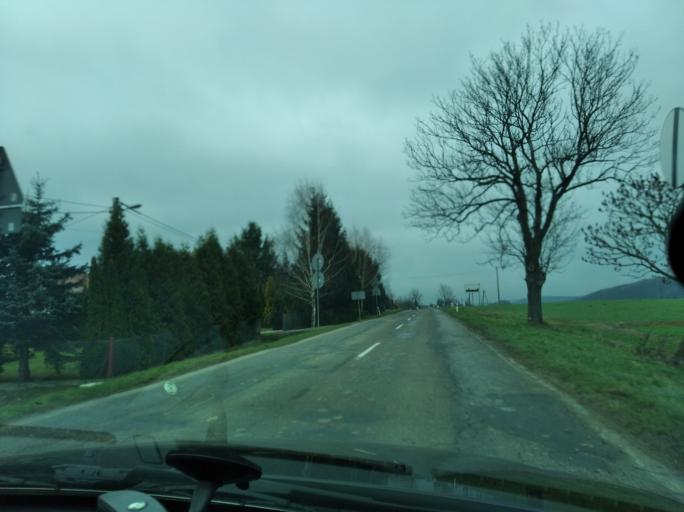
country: PL
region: Subcarpathian Voivodeship
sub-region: Powiat rzeszowski
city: Dynow
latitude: 49.8376
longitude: 22.2435
